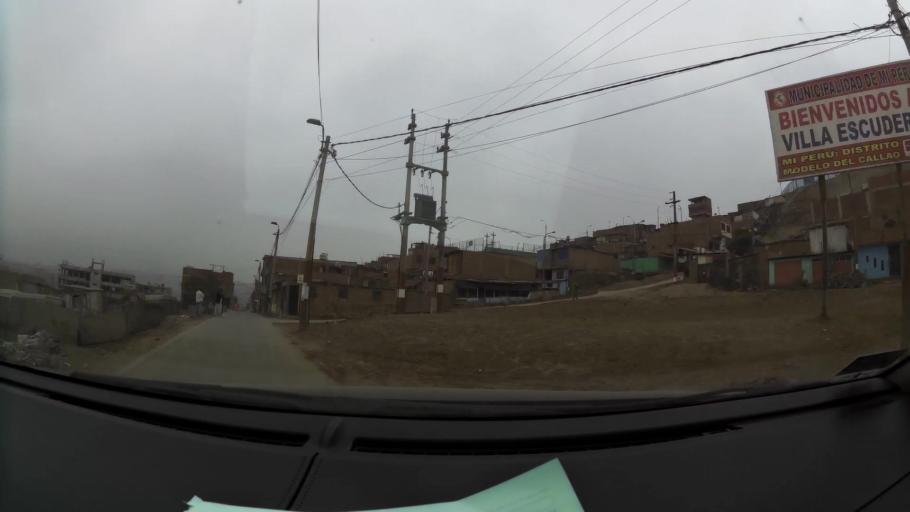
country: PE
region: Lima
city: Ventanilla
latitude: -11.8423
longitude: -77.1145
